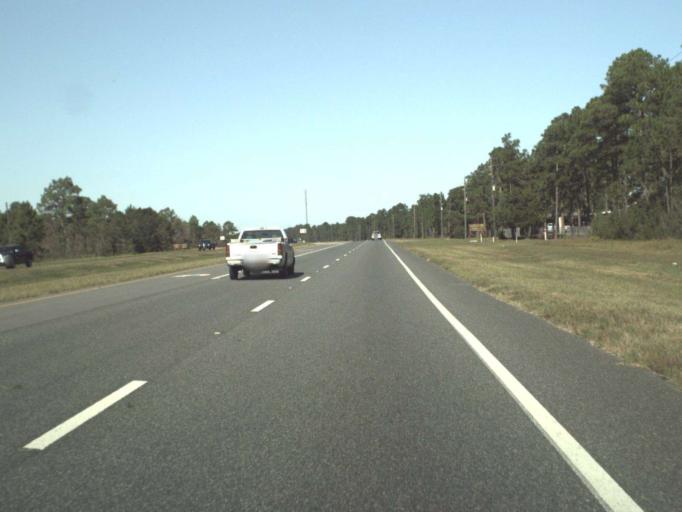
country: US
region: Florida
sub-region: Walton County
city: Seaside
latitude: 30.3516
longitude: -86.0848
